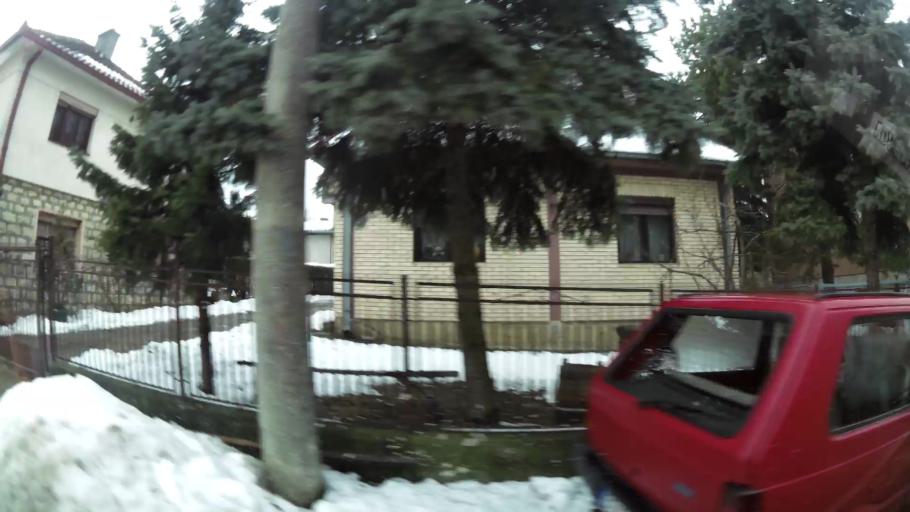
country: RS
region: Central Serbia
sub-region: Belgrade
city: Zvezdara
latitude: 44.7403
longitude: 20.5045
